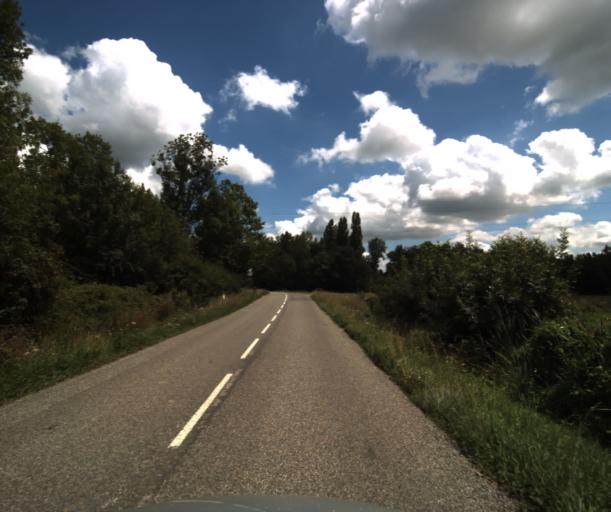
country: FR
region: Midi-Pyrenees
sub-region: Departement de la Haute-Garonne
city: Lacasse
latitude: 43.3978
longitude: 1.2738
